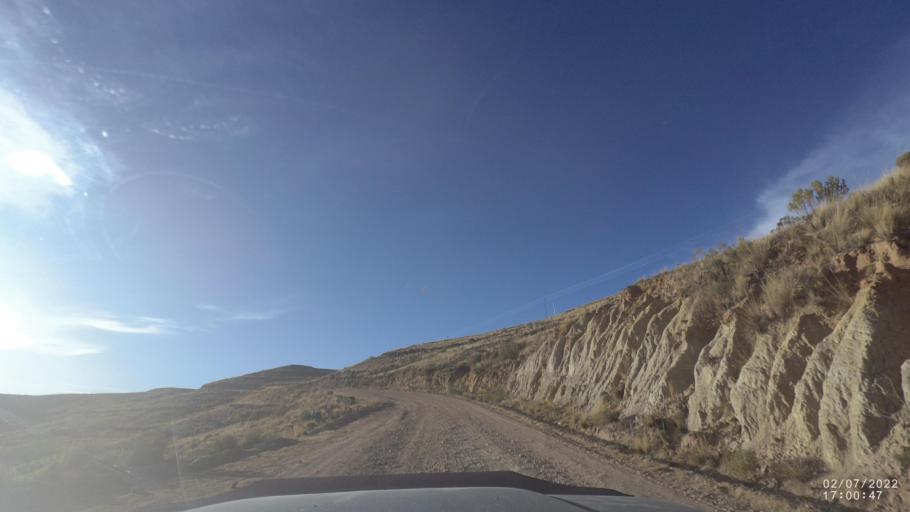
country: BO
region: Cochabamba
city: Irpa Irpa
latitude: -17.9359
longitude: -66.5545
